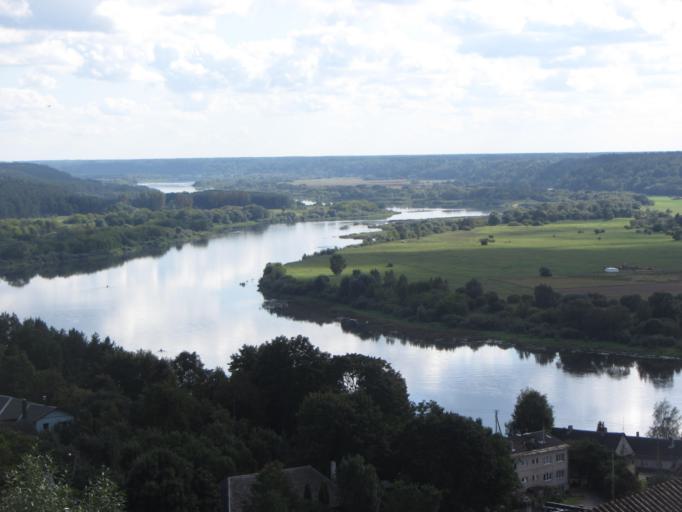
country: LT
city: Vilkija
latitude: 55.0402
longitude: 23.5833
